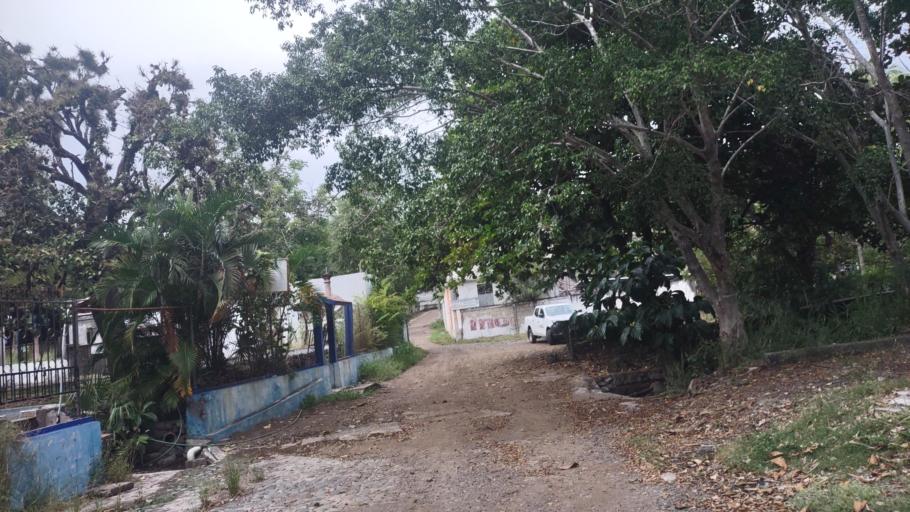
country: MX
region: Veracruz
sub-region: Actopan
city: Tinajitas
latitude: 19.6272
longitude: -96.4578
